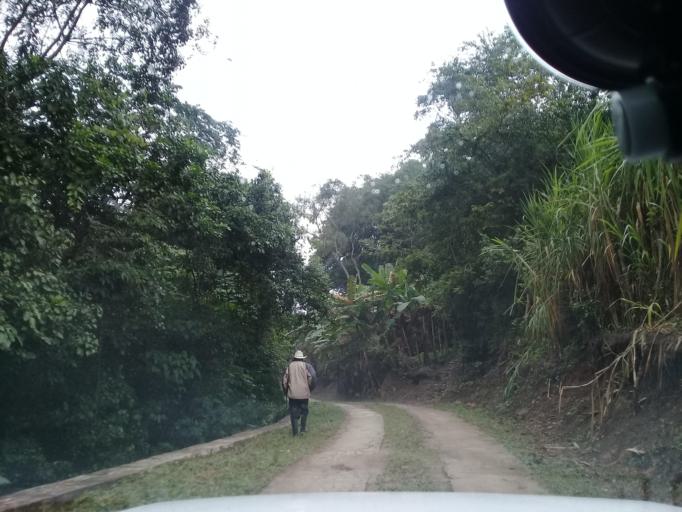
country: MX
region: Veracruz
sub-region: Chalma
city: San Pedro Coyutla
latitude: 21.2428
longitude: -98.4230
